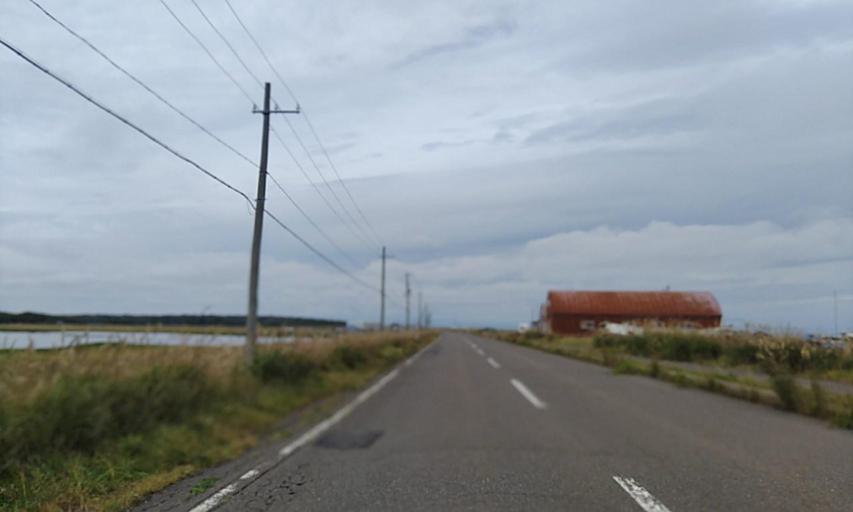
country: JP
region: Hokkaido
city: Shibetsu
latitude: 43.6029
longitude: 145.3030
